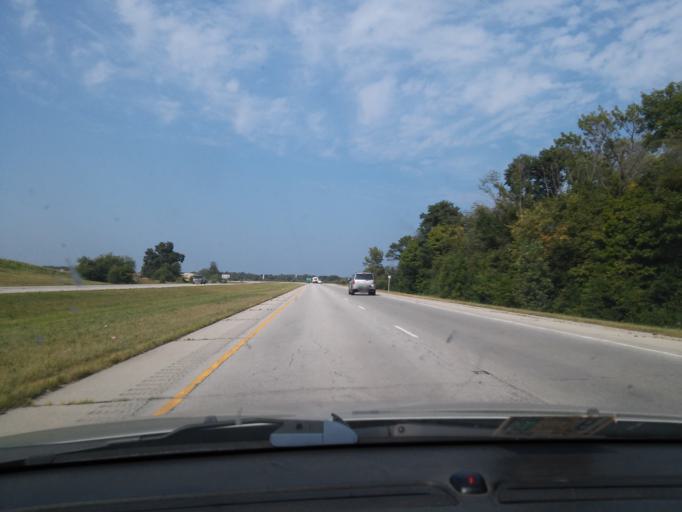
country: US
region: Ohio
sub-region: Greene County
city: Xenia
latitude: 39.6734
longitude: -83.9003
